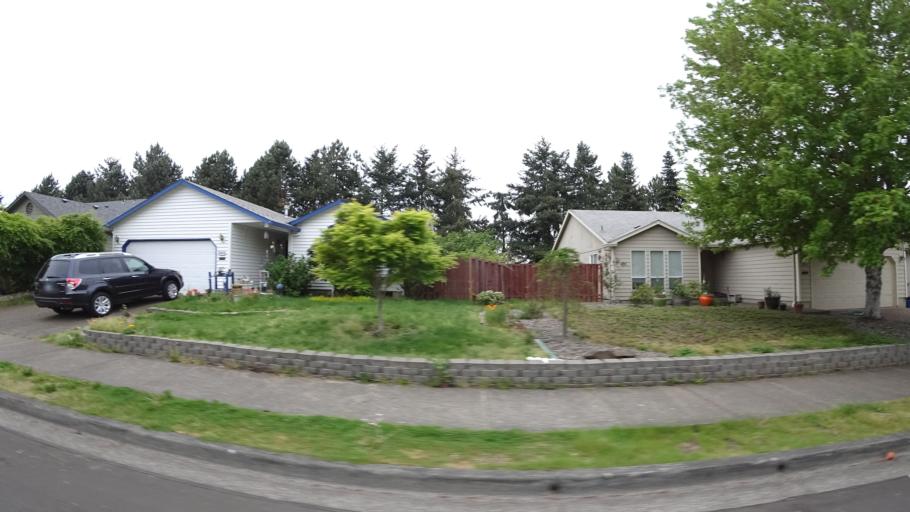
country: US
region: Oregon
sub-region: Washington County
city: Aloha
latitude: 45.5046
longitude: -122.9120
